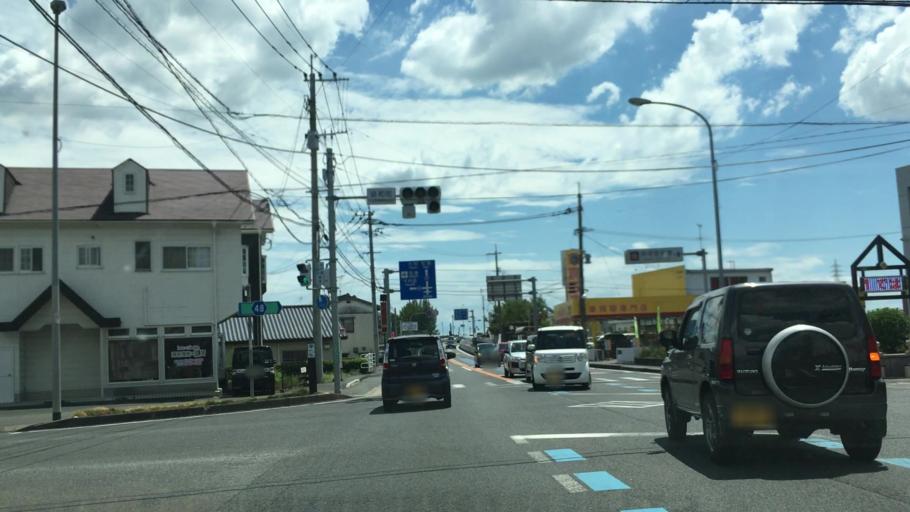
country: JP
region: Saga Prefecture
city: Kanzakimachi-kanzaki
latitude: 33.3074
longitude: 130.3702
